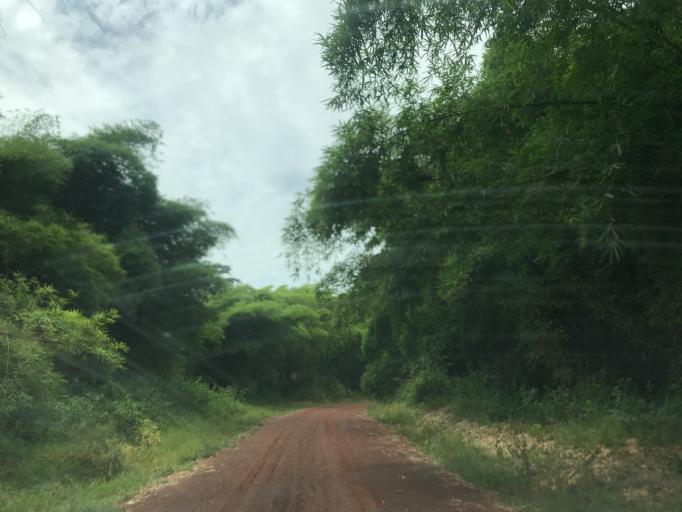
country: CD
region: Eastern Province
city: Buta
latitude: 2.4050
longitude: 24.9135
